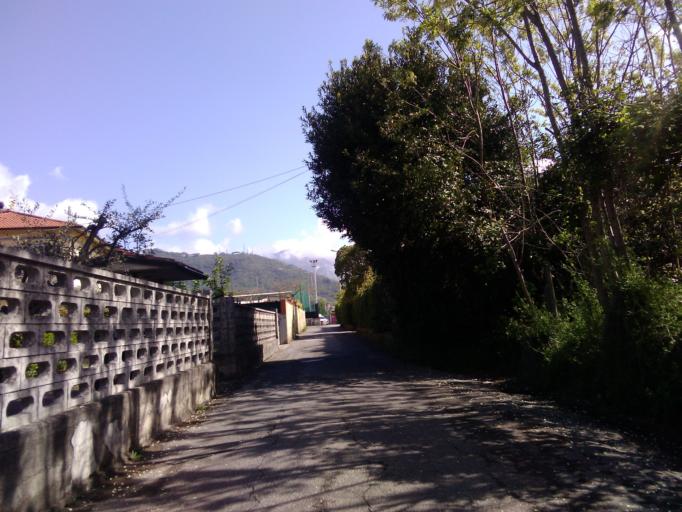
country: IT
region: Tuscany
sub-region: Provincia di Massa-Carrara
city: Marina di Carrara
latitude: 44.0513
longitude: 10.0455
